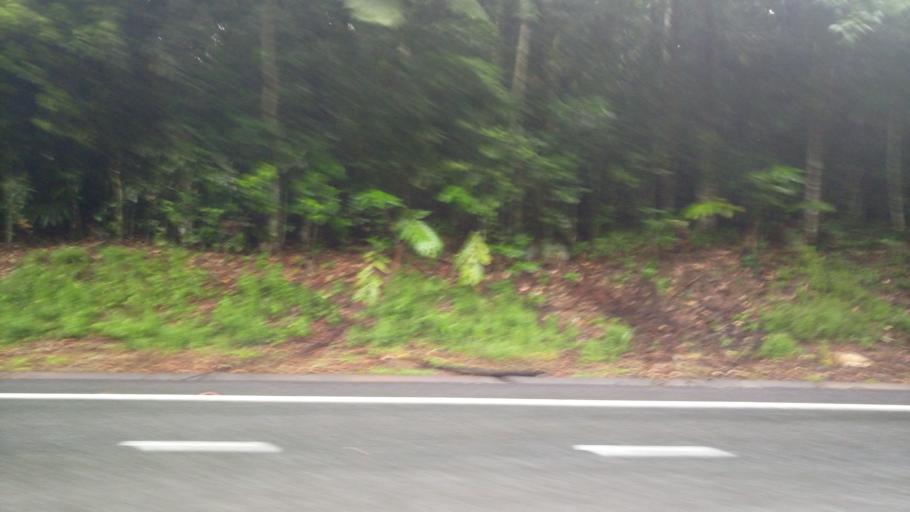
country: AU
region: Queensland
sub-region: Tablelands
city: Ravenshoe
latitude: -17.5848
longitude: 145.6983
